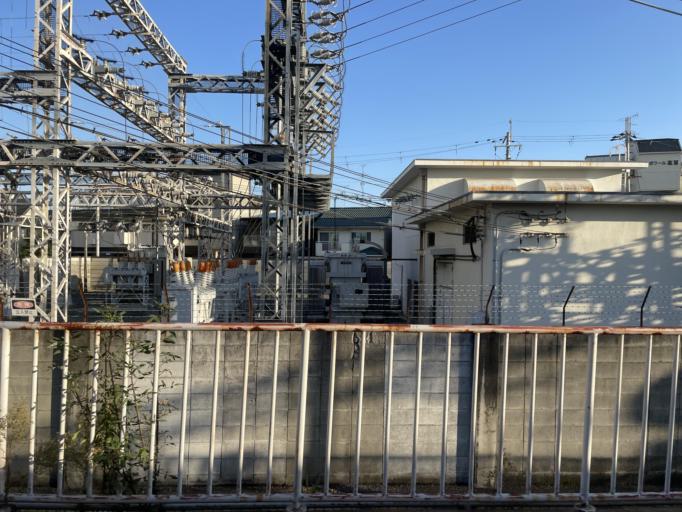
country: JP
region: Osaka
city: Kashihara
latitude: 34.5717
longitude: 135.5851
